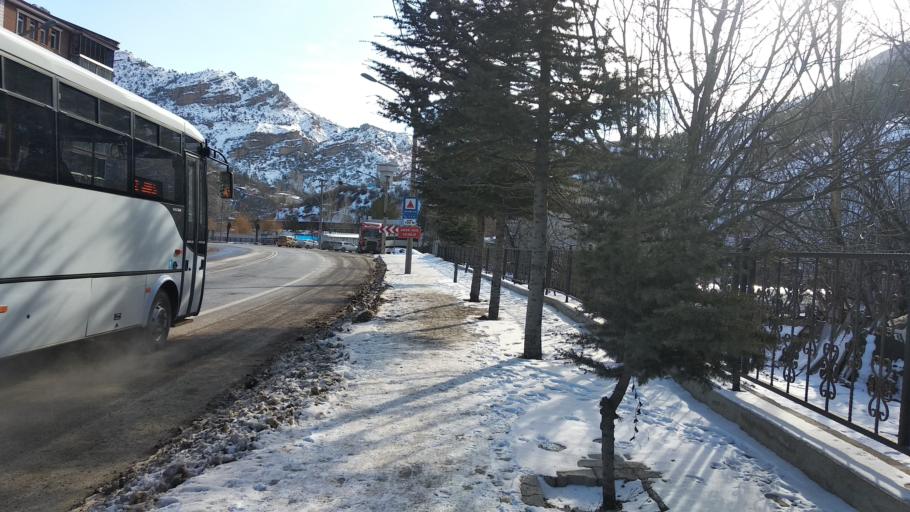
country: TR
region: Gumushane
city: Gumushkhane
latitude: 40.4478
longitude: 39.4975
